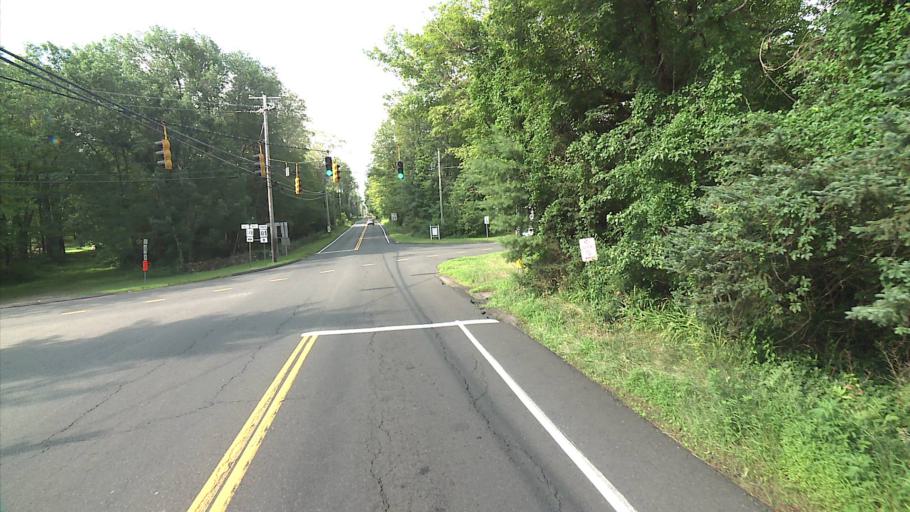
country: US
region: Connecticut
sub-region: Middlesex County
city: Higganum
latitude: 41.3908
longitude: -72.5627
